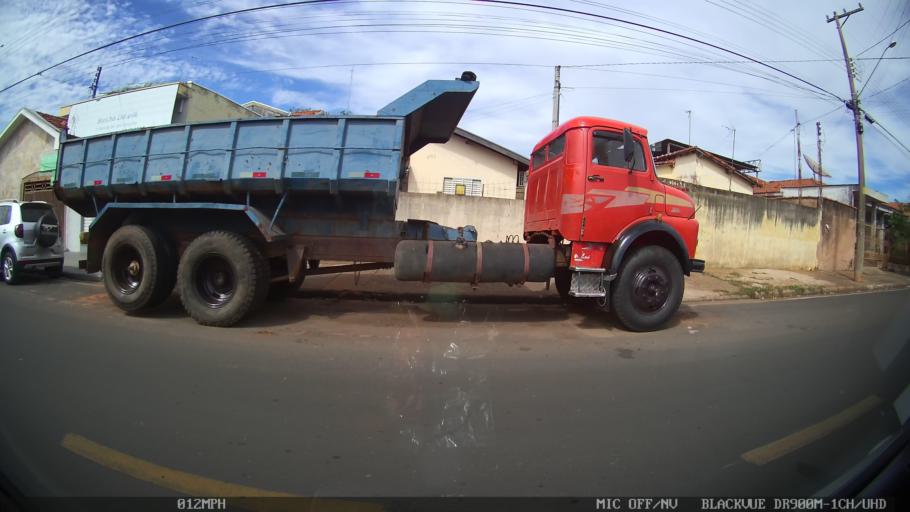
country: BR
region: Sao Paulo
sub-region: Catanduva
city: Catanduva
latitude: -21.1463
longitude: -48.9697
